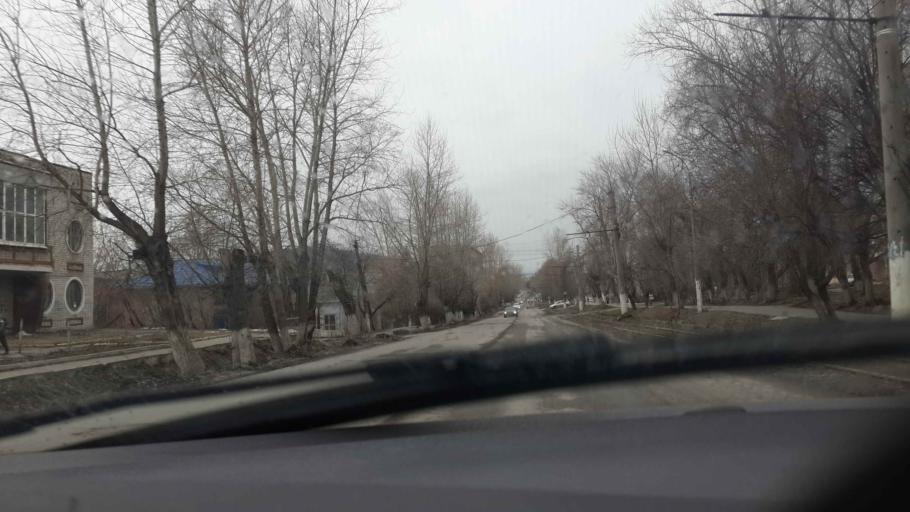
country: RU
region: Chelyabinsk
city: Zlatoust
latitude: 55.2016
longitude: 59.7243
